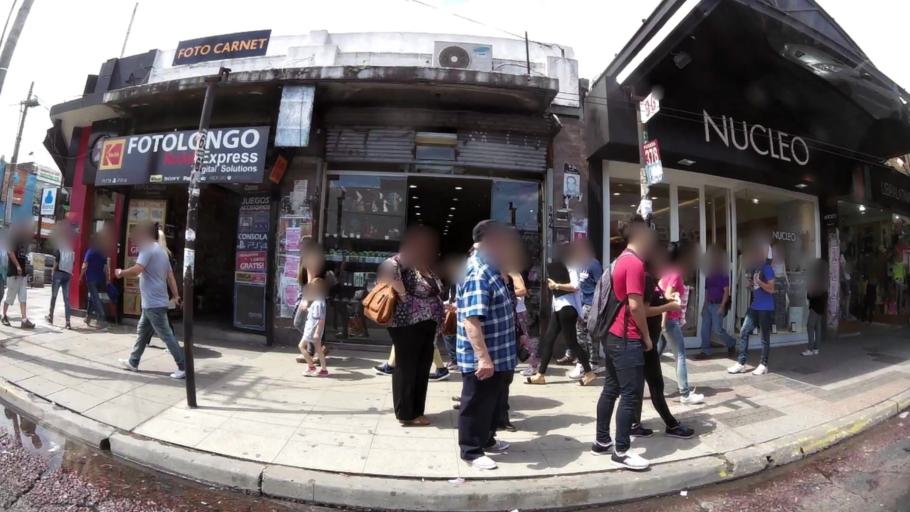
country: AR
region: Buenos Aires
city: San Justo
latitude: -34.6810
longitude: -58.5573
